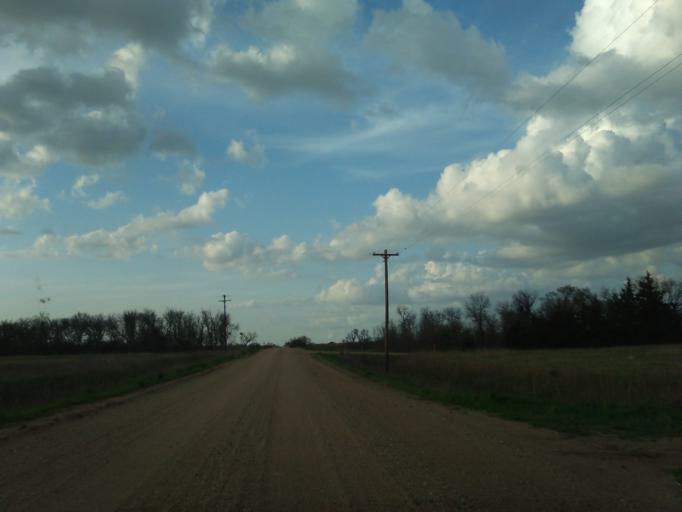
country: US
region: Nebraska
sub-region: Webster County
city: Red Cloud
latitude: 40.1751
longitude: -98.4437
